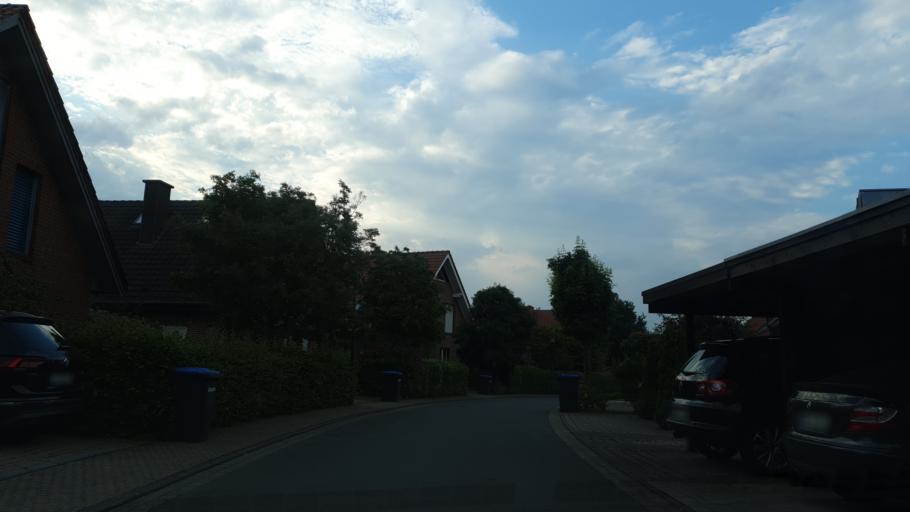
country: DE
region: North Rhine-Westphalia
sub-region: Regierungsbezirk Munster
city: Ostbevern
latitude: 52.0359
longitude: 7.8317
